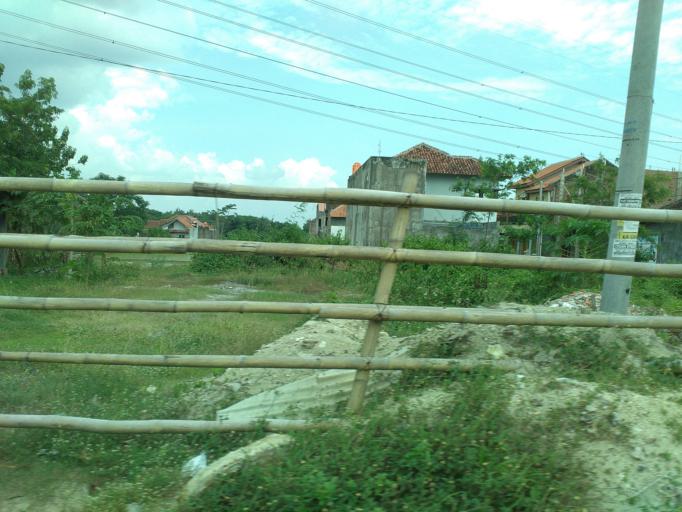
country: ID
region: Central Java
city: Karanganom
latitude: -7.6830
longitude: 110.6352
